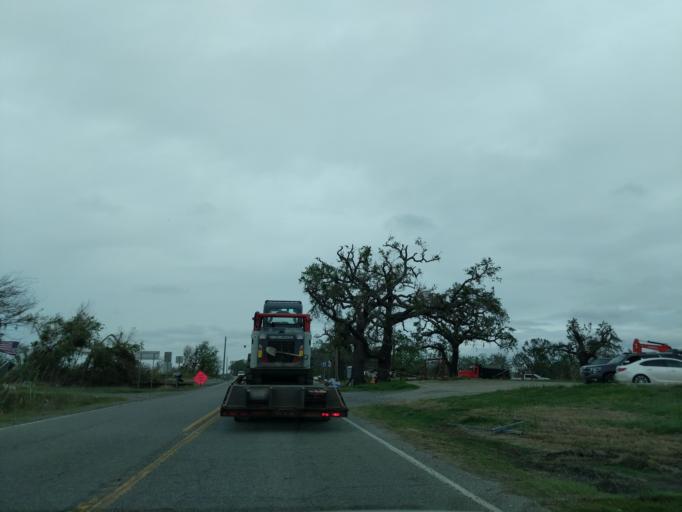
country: US
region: Louisiana
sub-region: Cameron Parish
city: Cameron
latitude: 29.7860
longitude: -93.1131
